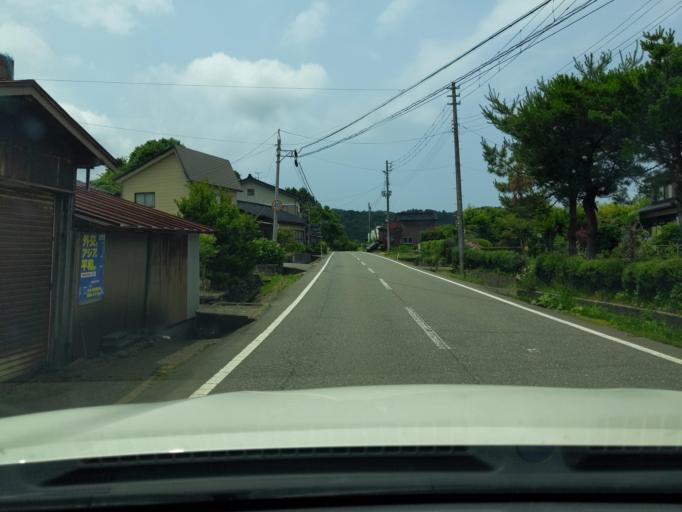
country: JP
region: Niigata
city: Kashiwazaki
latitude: 37.3323
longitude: 138.5610
